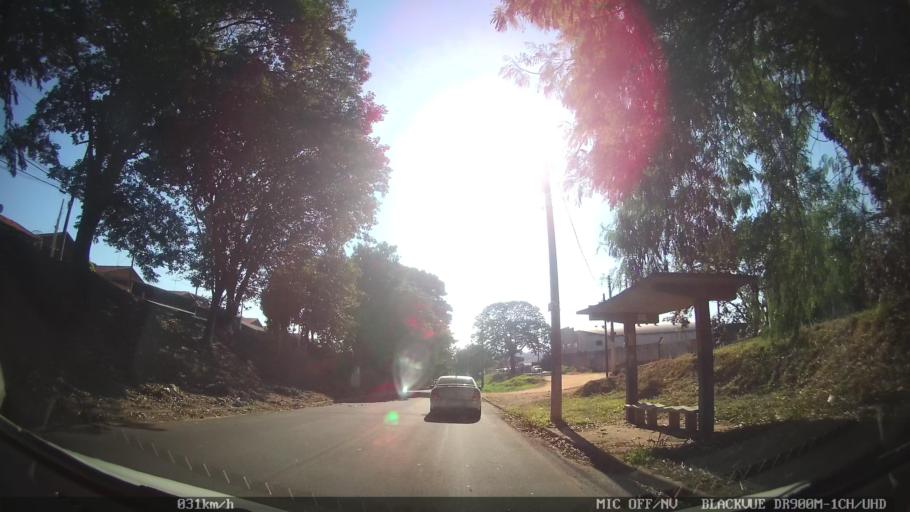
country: BR
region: Sao Paulo
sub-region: Campinas
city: Campinas
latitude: -22.9661
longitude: -47.1091
